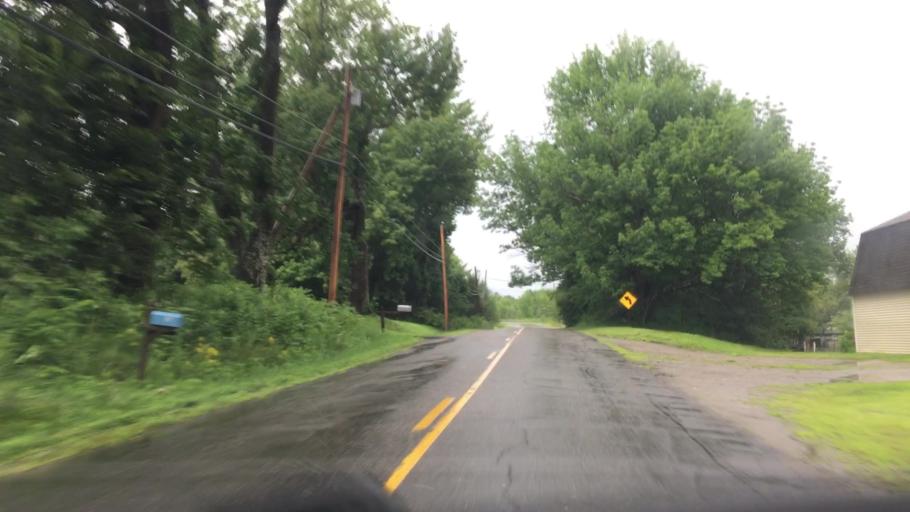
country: US
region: Maine
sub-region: Kennebec County
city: Gardiner
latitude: 44.2140
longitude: -69.8036
